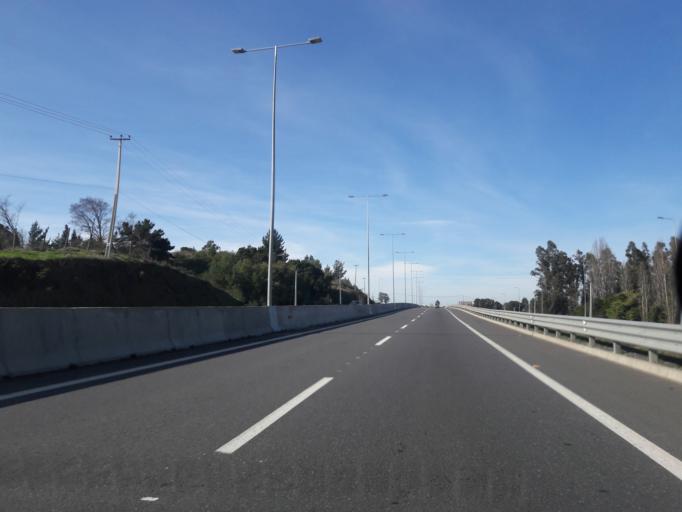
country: CL
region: Biobio
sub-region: Provincia de Biobio
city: Yumbel
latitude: -37.0001
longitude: -72.5671
